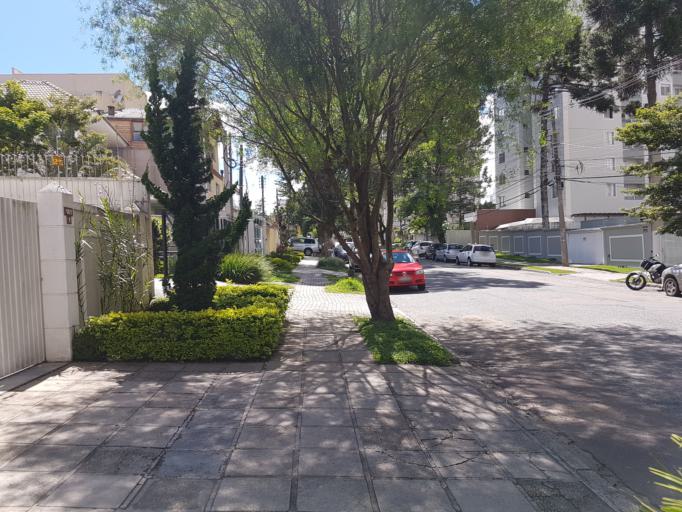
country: BR
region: Parana
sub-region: Curitiba
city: Curitiba
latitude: -25.4360
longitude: -49.2403
